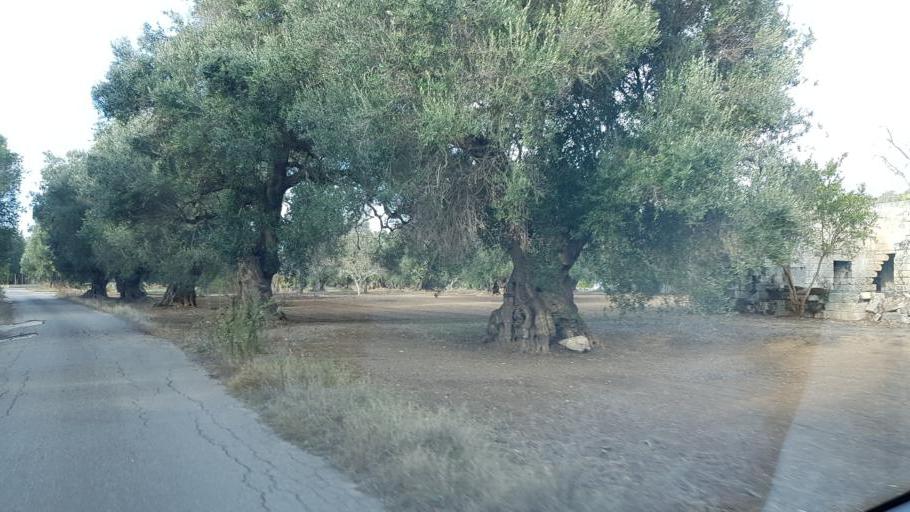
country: IT
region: Apulia
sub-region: Provincia di Brindisi
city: Oria
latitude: 40.5063
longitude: 17.6717
